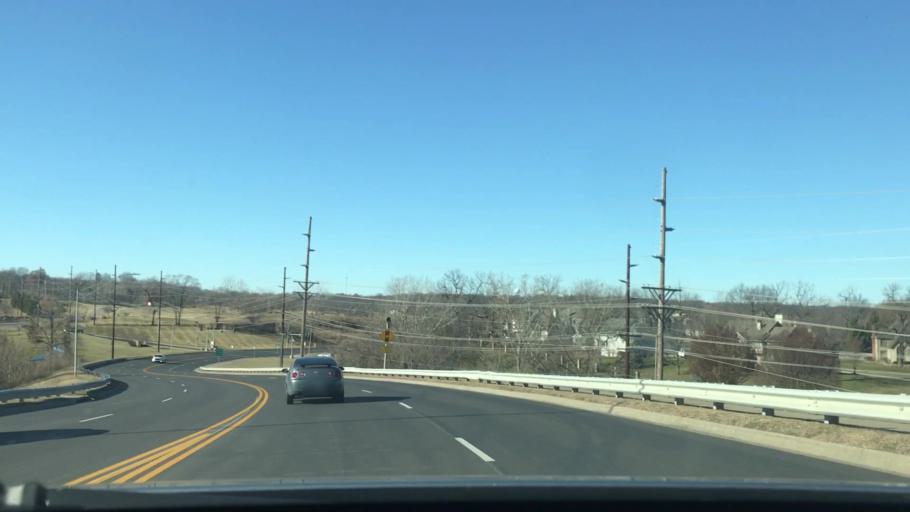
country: US
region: Missouri
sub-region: Jackson County
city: Independence
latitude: 39.0559
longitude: -94.3883
